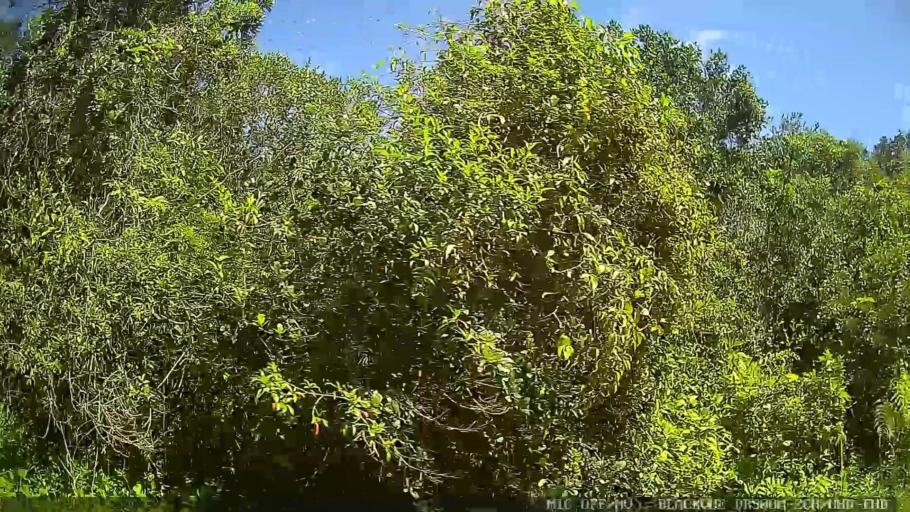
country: BR
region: Sao Paulo
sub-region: Itanhaem
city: Itanhaem
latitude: -24.2280
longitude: -46.8880
